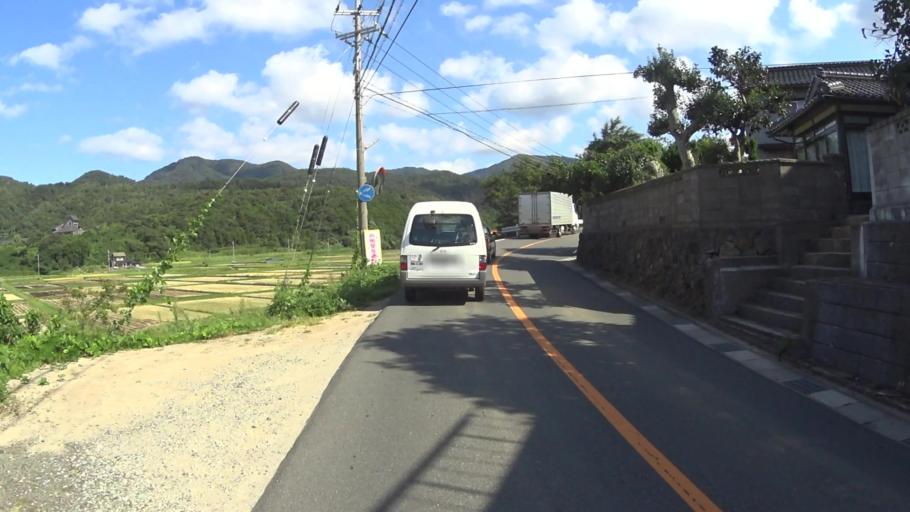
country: JP
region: Kyoto
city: Miyazu
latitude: 35.7536
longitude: 135.1721
